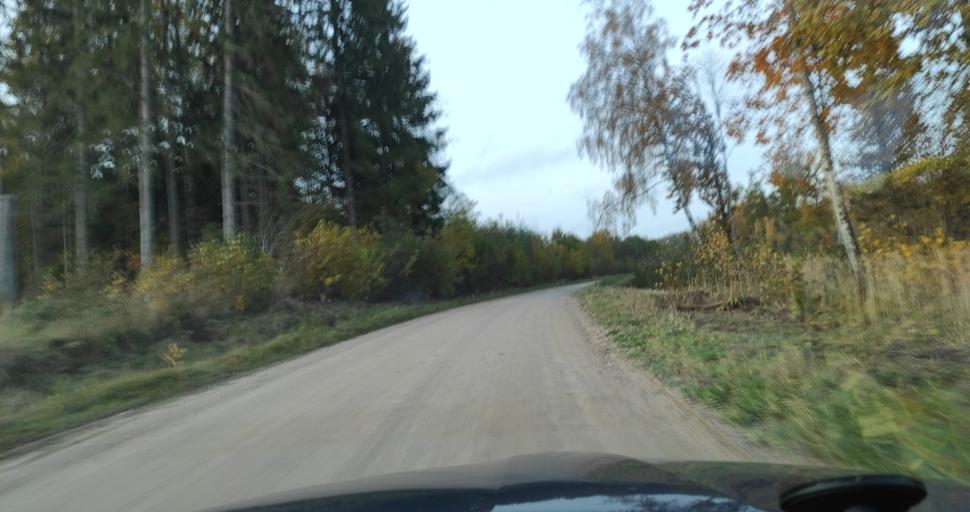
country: LV
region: Vainode
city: Vainode
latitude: 56.6340
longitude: 21.8127
